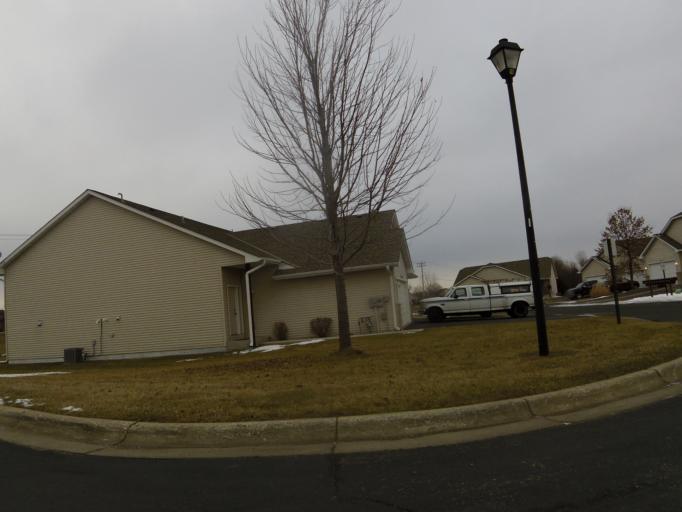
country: US
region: Minnesota
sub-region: Carver County
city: Waconia
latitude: 44.8546
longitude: -93.8152
